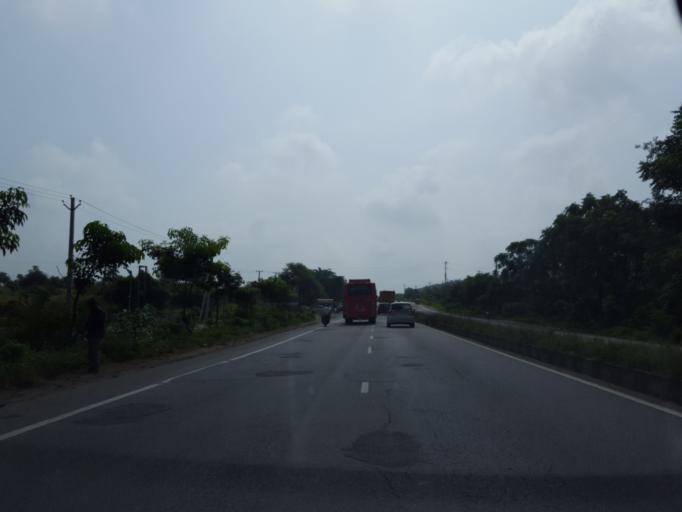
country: IN
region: Telangana
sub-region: Rangareddi
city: Ghatkesar
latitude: 17.2866
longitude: 78.7730
